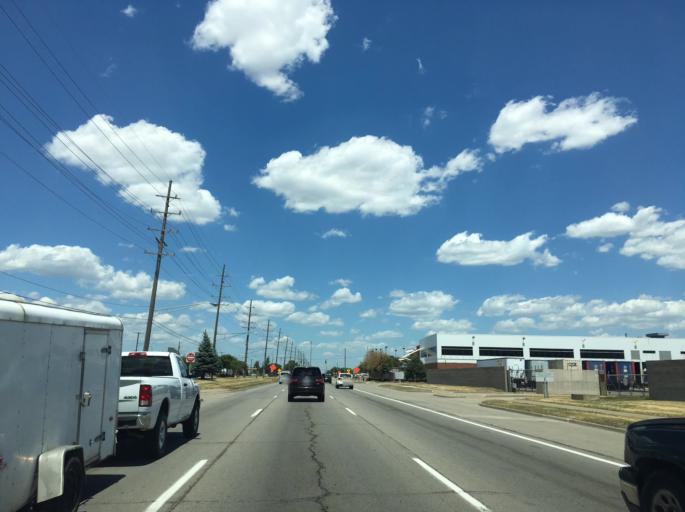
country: US
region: Michigan
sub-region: Macomb County
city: Warren
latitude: 42.4577
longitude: -83.0445
